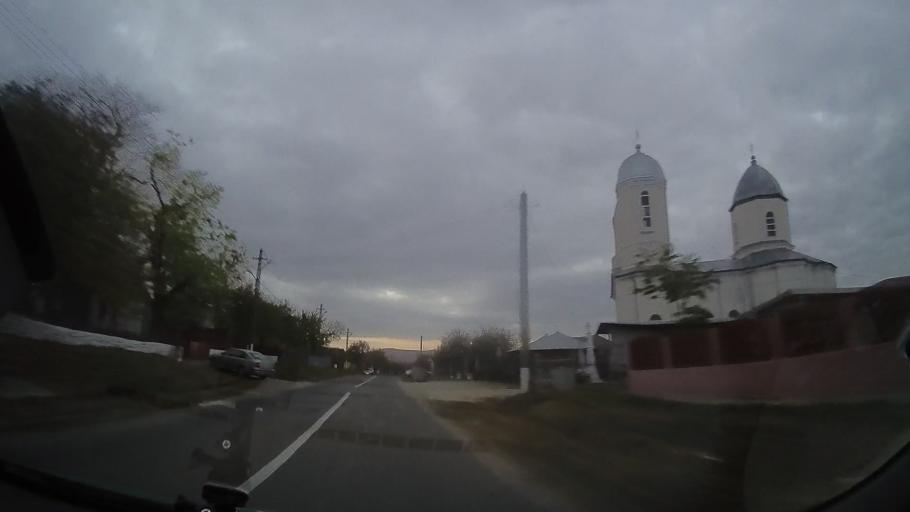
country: RO
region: Tulcea
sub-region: Comuna Mihai Bravu
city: Turda
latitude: 44.9757
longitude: 28.6215
